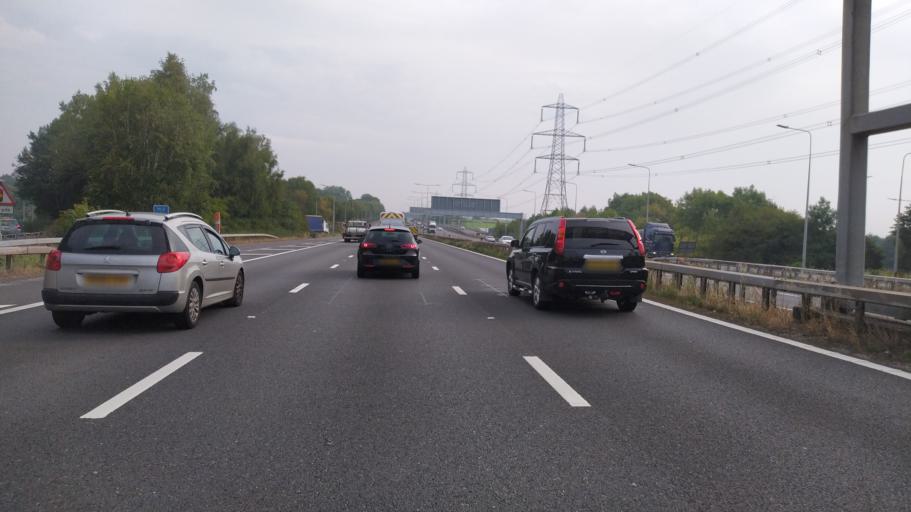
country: GB
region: England
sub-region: Hampshire
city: Eastleigh
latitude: 50.9723
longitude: -1.3776
